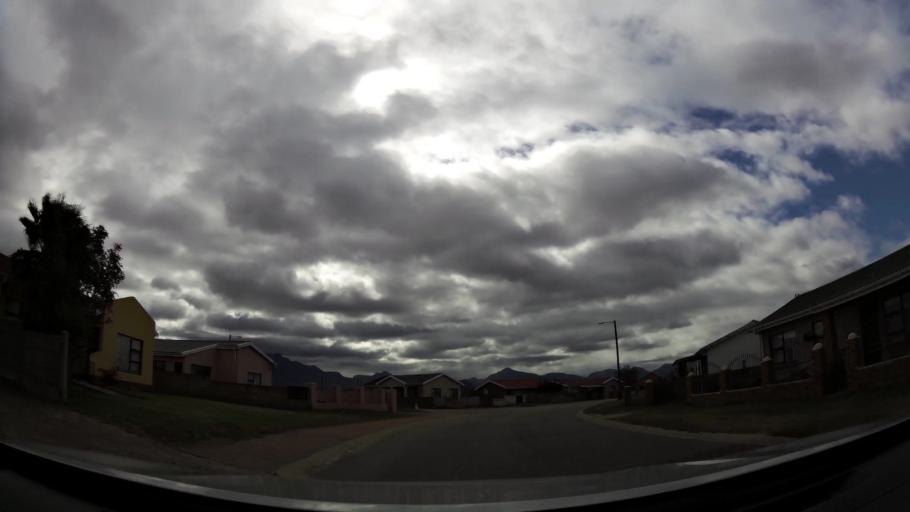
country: ZA
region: Western Cape
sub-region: Eden District Municipality
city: George
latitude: -34.0176
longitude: 22.4698
